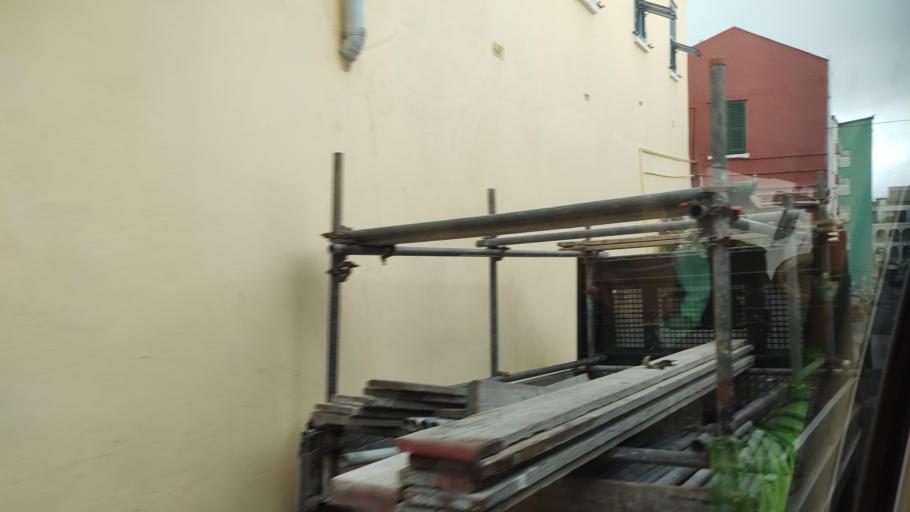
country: GI
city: Gibraltar
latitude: 36.1413
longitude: -5.3504
